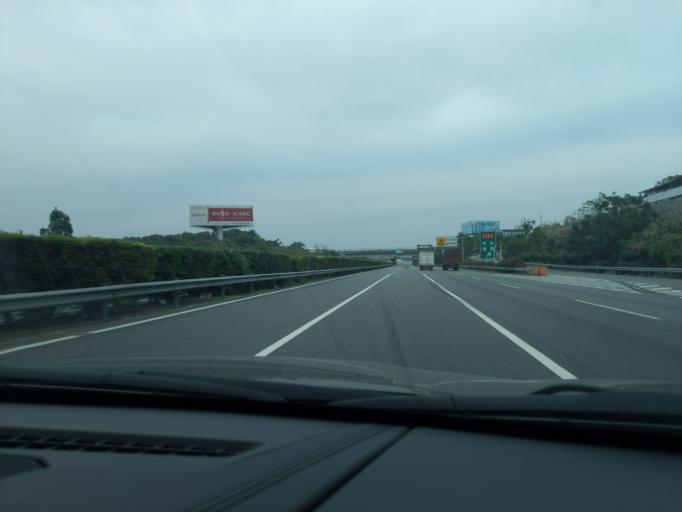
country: CN
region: Fujian
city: Anhai
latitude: 24.7279
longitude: 118.4129
